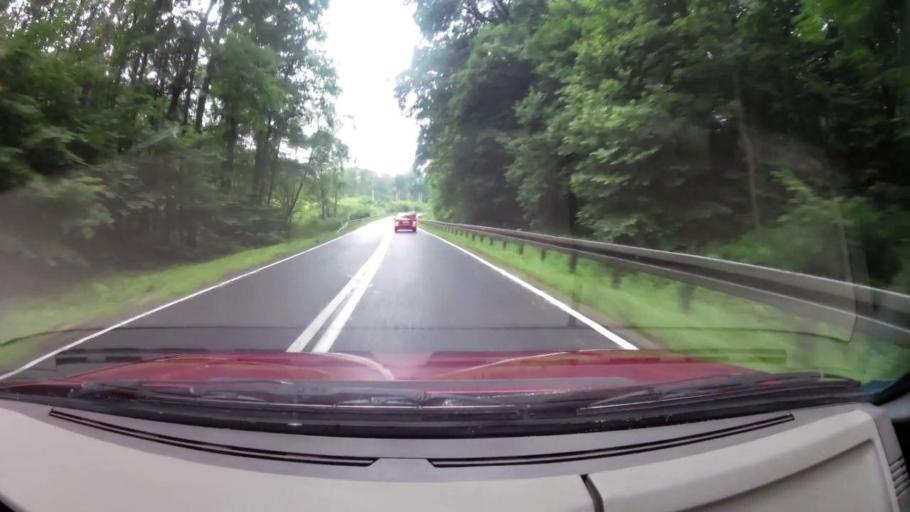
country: PL
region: West Pomeranian Voivodeship
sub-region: Powiat stargardzki
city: Marianowo
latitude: 53.4210
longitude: 15.2758
